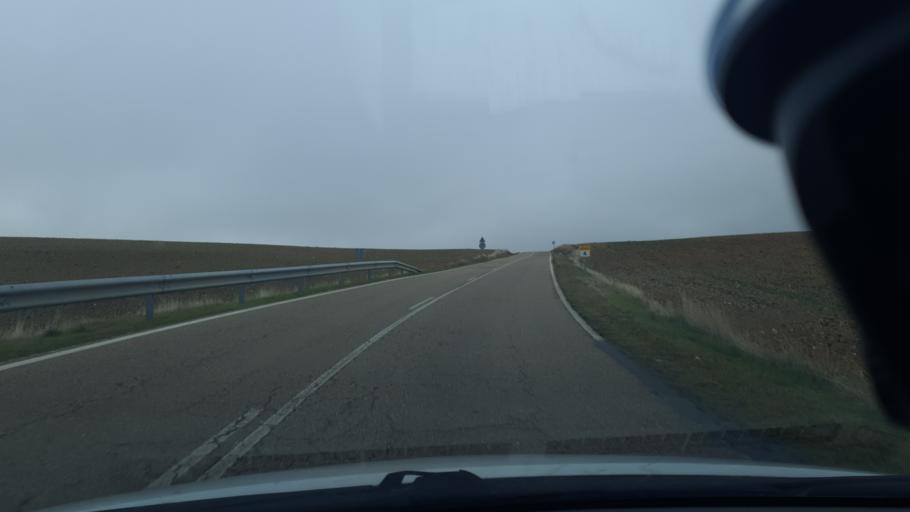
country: ES
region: Castille and Leon
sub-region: Provincia de Segovia
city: Hontanares de Eresma
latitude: 40.9920
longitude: -4.1976
